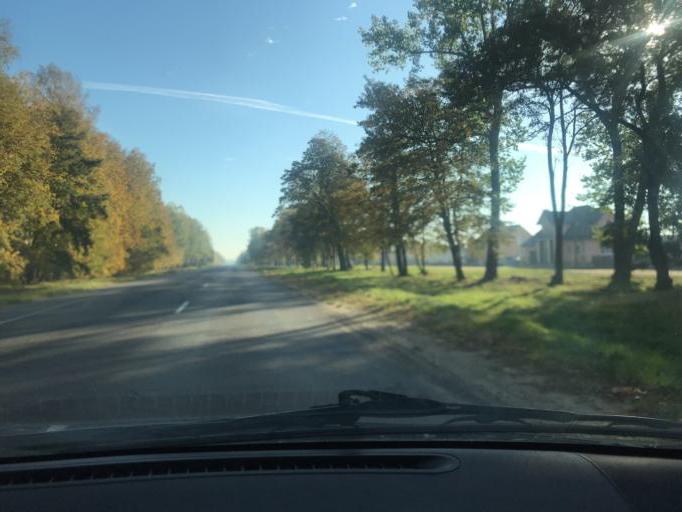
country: BY
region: Brest
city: Ivanava
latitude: 52.1444
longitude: 25.4960
